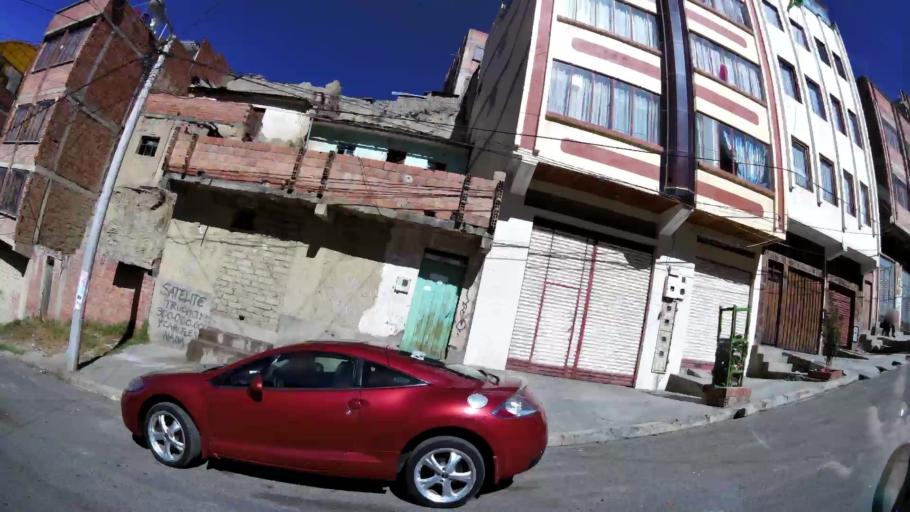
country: BO
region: La Paz
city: La Paz
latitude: -16.5040
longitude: -68.1486
